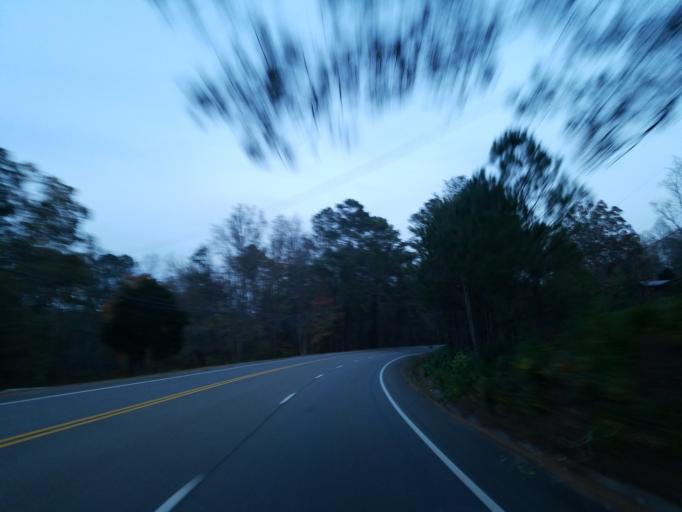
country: US
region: Georgia
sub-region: Pickens County
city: Jasper
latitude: 34.5098
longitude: -84.4958
